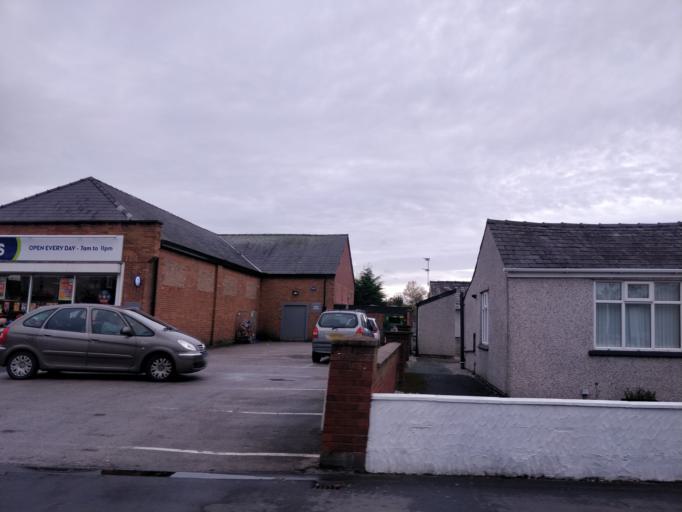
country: GB
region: England
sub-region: Sefton
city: Southport
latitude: 53.6677
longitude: -2.9709
